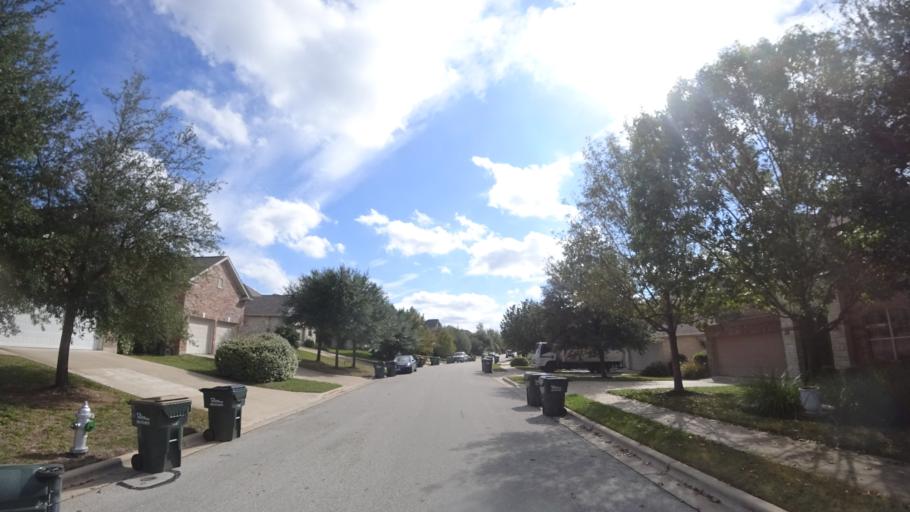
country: US
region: Texas
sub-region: Travis County
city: Hudson Bend
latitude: 30.3642
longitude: -97.9050
